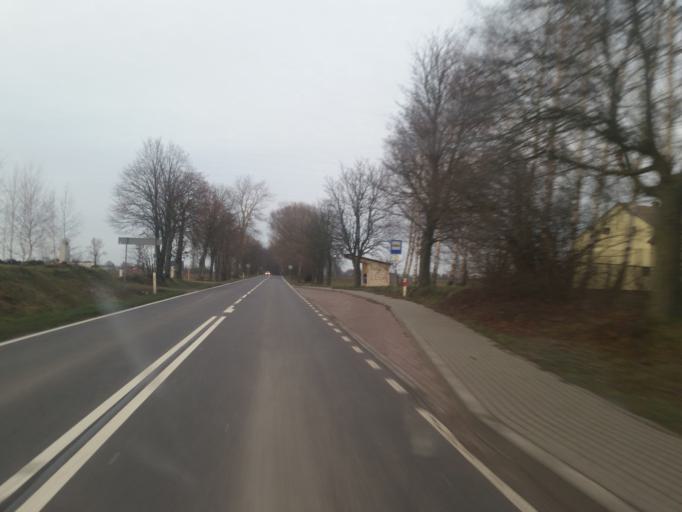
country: PL
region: Kujawsko-Pomorskie
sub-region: Powiat brodnicki
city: Brodnica
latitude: 53.1818
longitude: 19.3893
